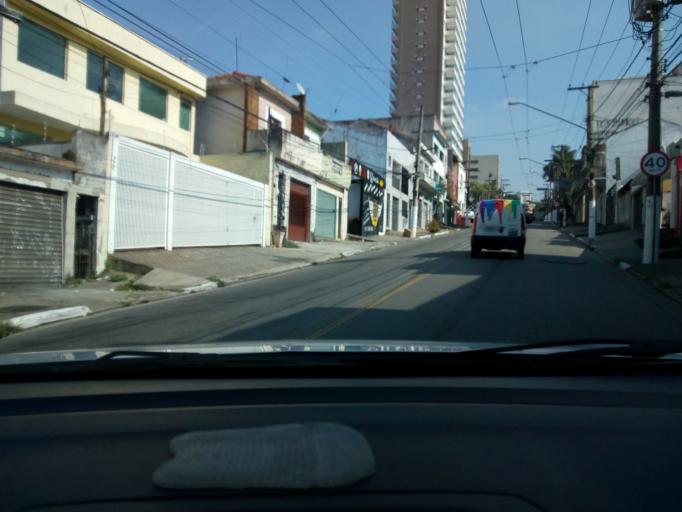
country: BR
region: Sao Paulo
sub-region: Sao Paulo
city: Sao Paulo
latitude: -23.5809
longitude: -46.6156
